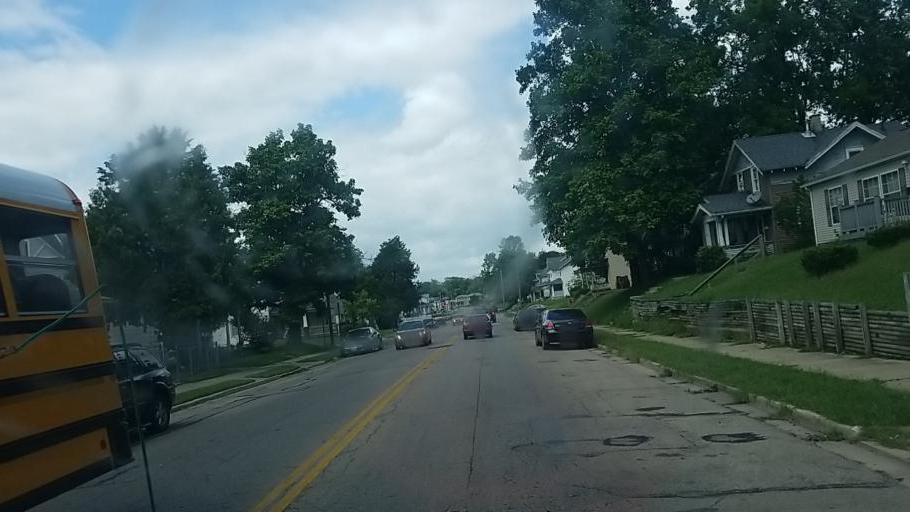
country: US
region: Ohio
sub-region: Clark County
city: Springfield
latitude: 39.9089
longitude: -83.7937
